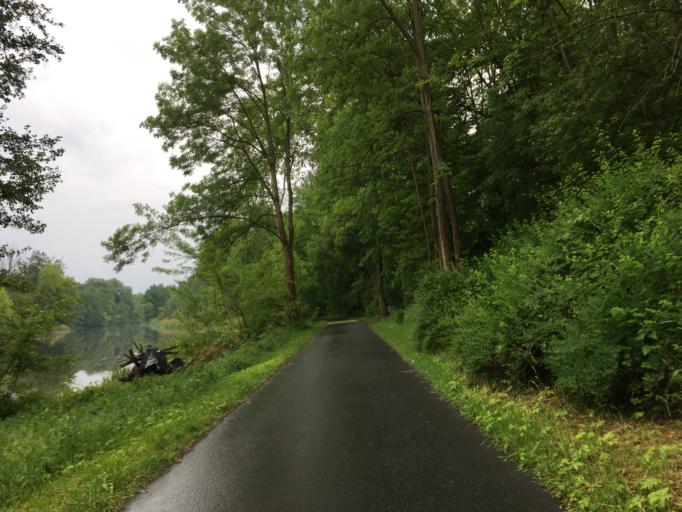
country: DE
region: Brandenburg
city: Eberswalde
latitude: 52.8439
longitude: 13.7817
